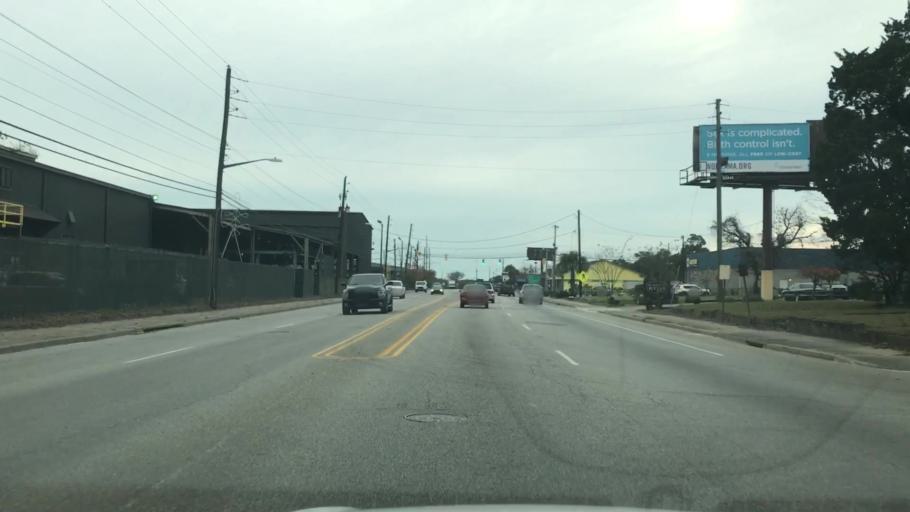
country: US
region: South Carolina
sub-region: Georgetown County
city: Georgetown
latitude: 33.3677
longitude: -79.2932
